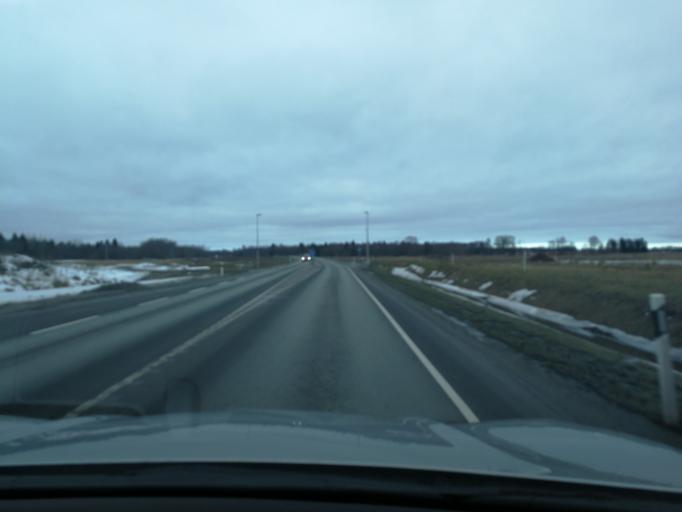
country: EE
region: Harju
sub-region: Saku vald
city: Saku
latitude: 59.3199
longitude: 24.6409
